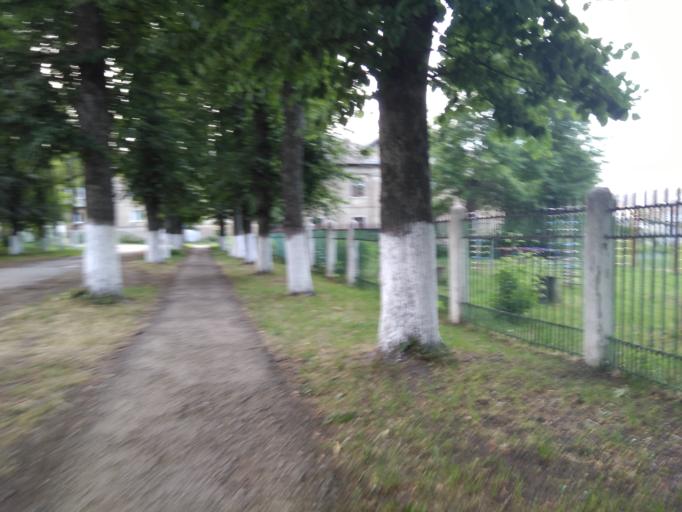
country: RU
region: Tula
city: Lomintsevskiy
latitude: 53.9344
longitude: 37.6261
